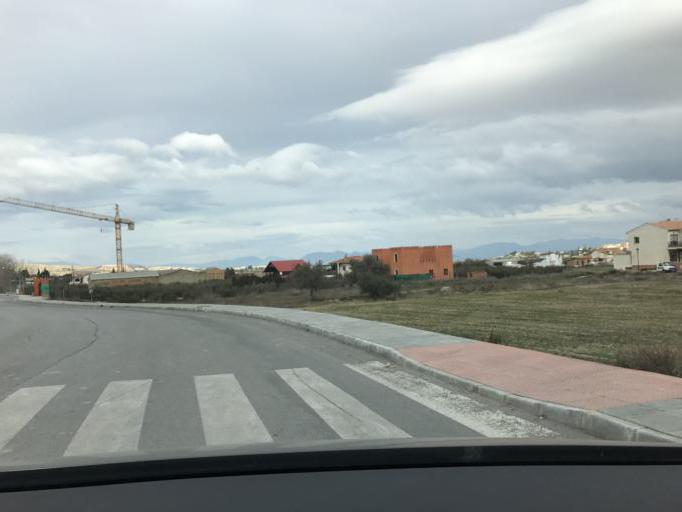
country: ES
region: Andalusia
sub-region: Provincia de Granada
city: Alhendin
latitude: 37.1025
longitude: -3.6515
